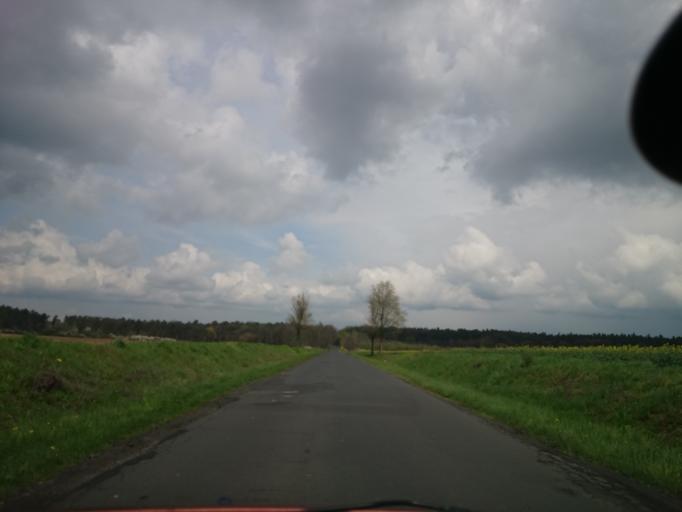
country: PL
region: Opole Voivodeship
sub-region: Powiat strzelecki
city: Izbicko
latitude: 50.5327
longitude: 18.1322
